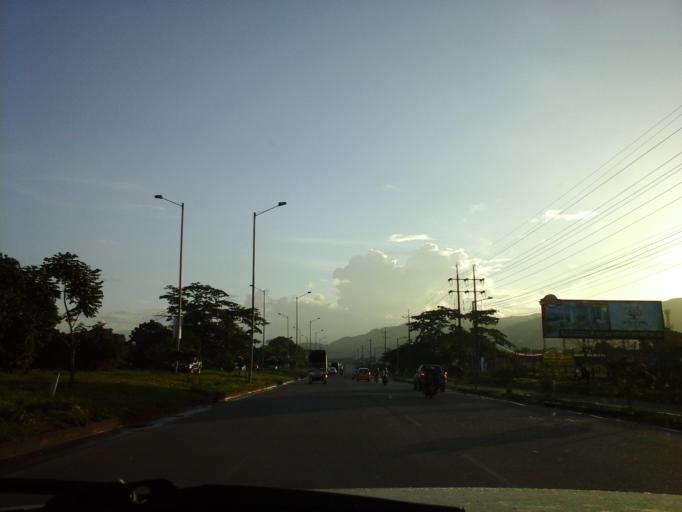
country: CO
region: Meta
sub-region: Villavicencio
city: Villavicencio
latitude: 4.1173
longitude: -73.6242
